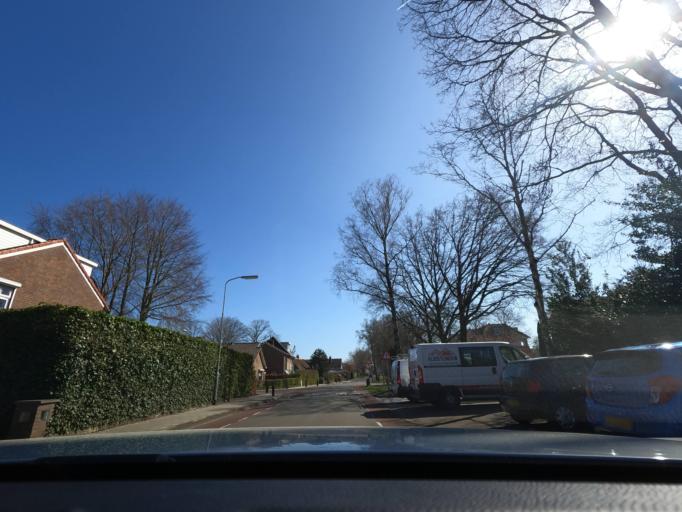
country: NL
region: Gelderland
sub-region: Gemeente Oldebroek
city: Oldebroek
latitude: 52.4152
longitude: 5.8771
